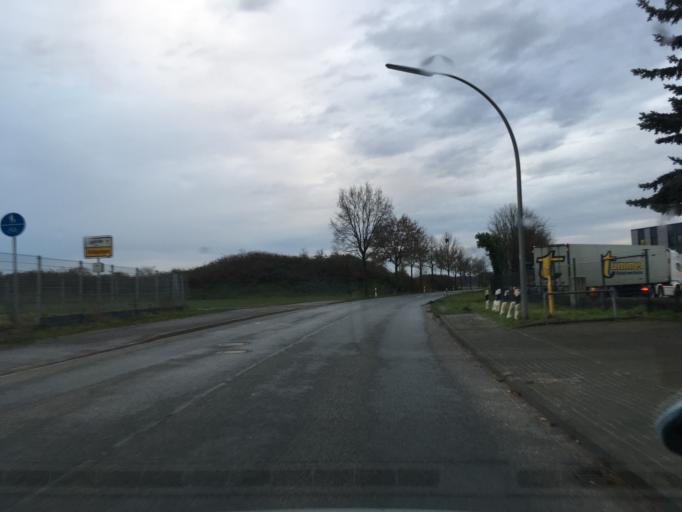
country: DE
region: North Rhine-Westphalia
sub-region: Regierungsbezirk Munster
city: Schoppingen
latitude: 52.0853
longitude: 7.2328
